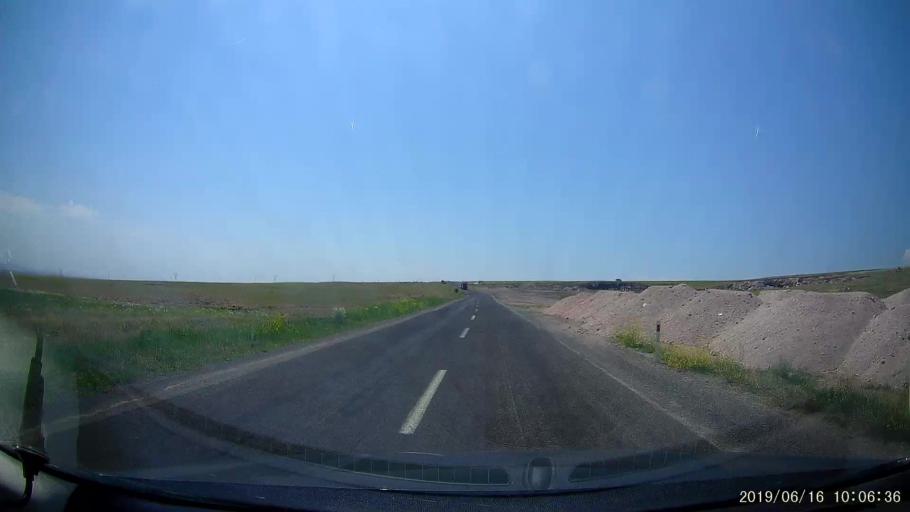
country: TR
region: Kars
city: Digor
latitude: 40.2534
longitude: 43.5441
